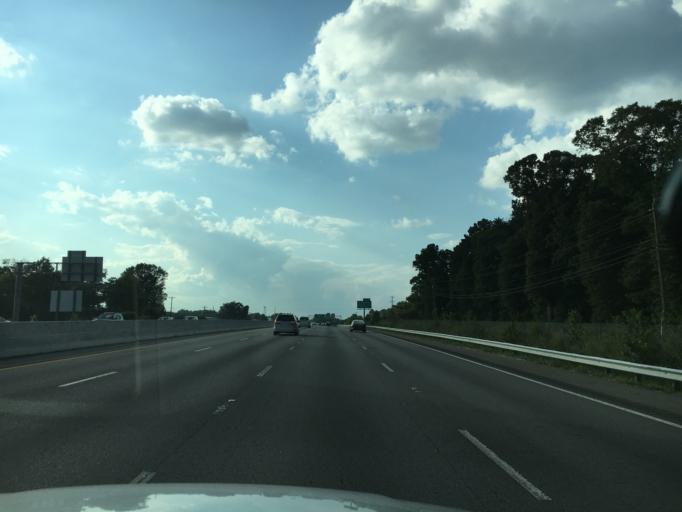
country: US
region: South Carolina
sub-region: Greenville County
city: Simpsonville
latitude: 34.7453
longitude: -82.2787
